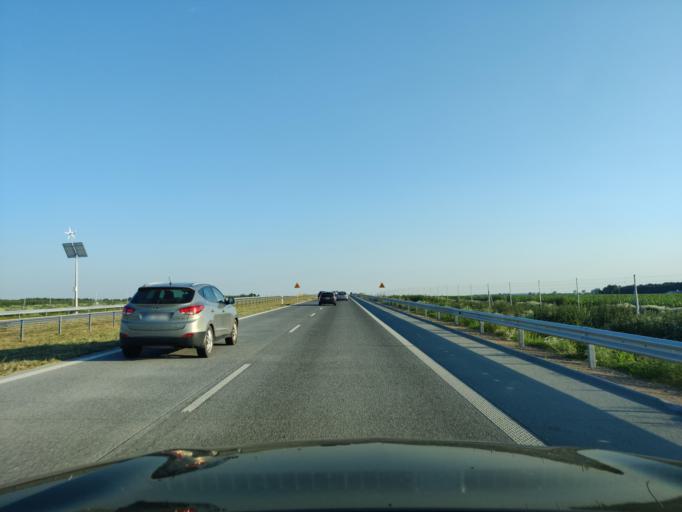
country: PL
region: Masovian Voivodeship
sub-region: Powiat mlawski
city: Wisniewo
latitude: 53.0525
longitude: 20.3619
